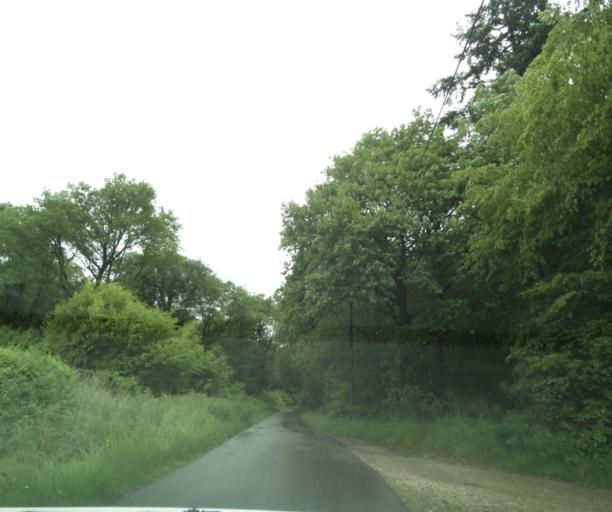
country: FR
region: Bourgogne
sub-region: Departement de Saone-et-Loire
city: Ciry-le-Noble
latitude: 46.5200
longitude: 4.3018
